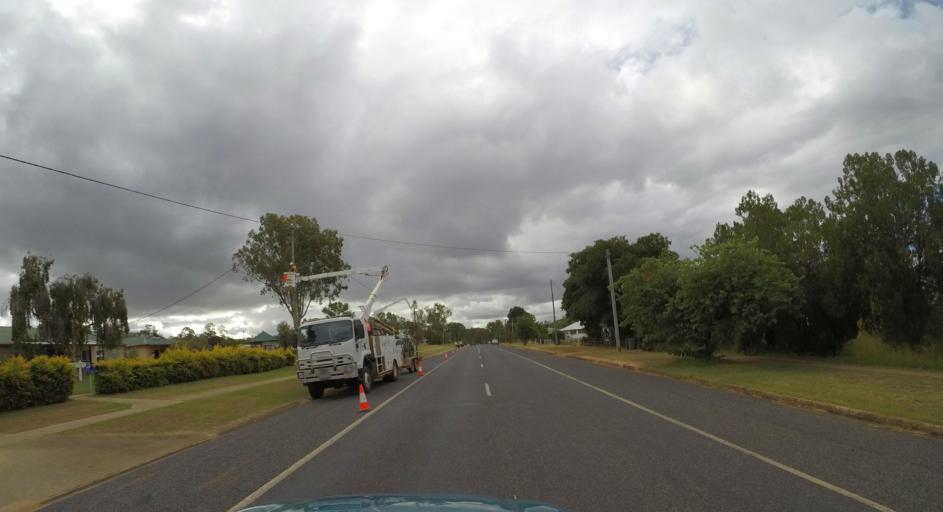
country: AU
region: Queensland
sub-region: North Burnett
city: Gayndah
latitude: -25.3674
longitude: 151.1213
